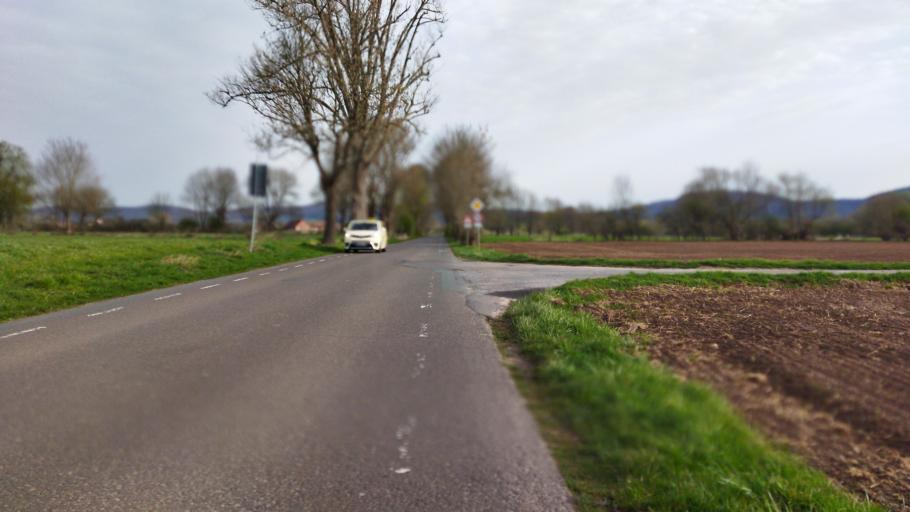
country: DE
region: Lower Saxony
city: Rinteln
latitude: 52.1870
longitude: 9.0269
